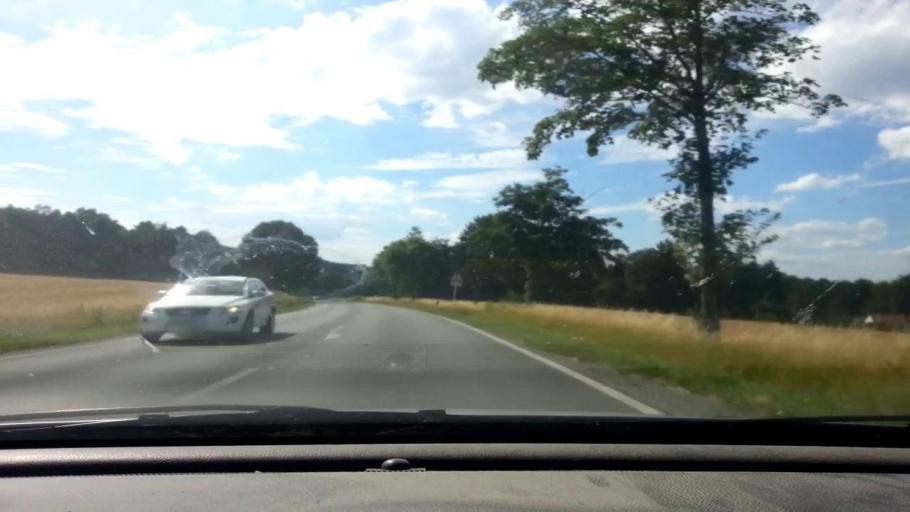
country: DE
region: Bavaria
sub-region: Upper Franconia
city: Neunkirchen am Main
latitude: 49.9177
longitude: 11.6492
